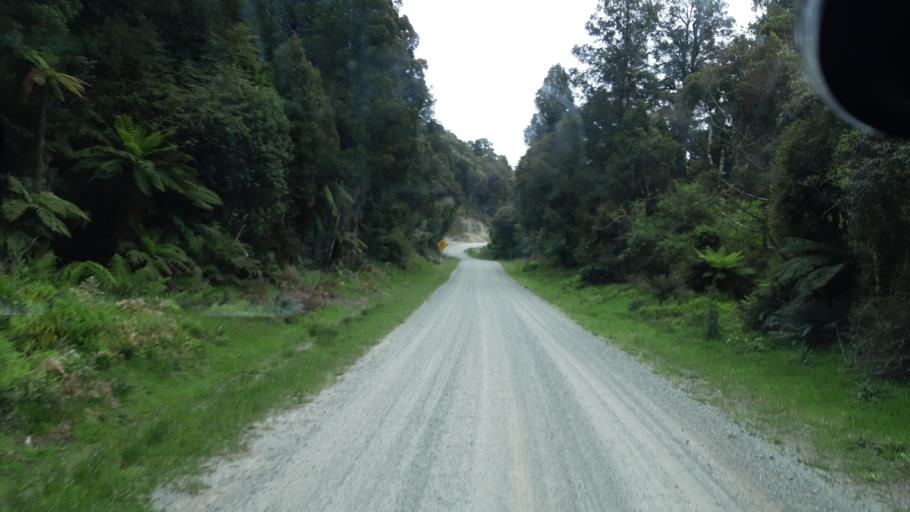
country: NZ
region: West Coast
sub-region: Grey District
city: Greymouth
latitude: -42.6410
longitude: 171.2981
